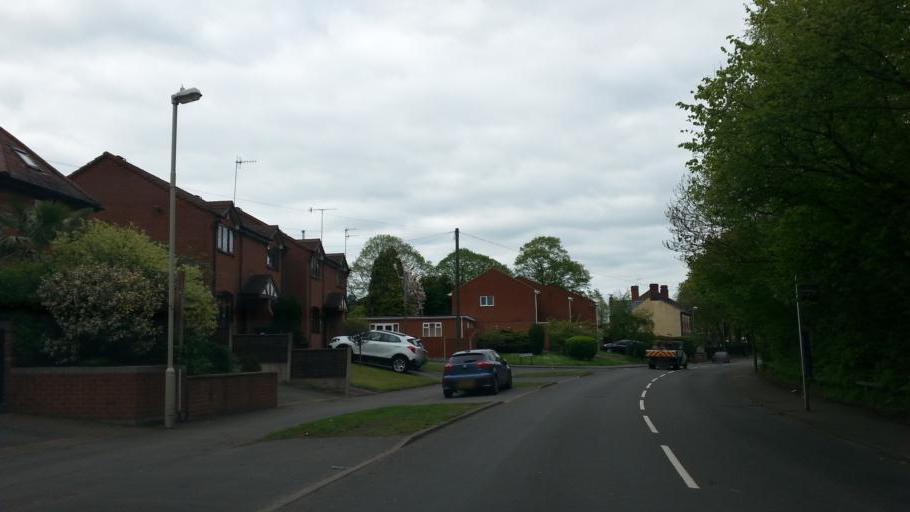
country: GB
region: England
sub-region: Dudley
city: Kingswinford
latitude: 52.4785
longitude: -2.1676
